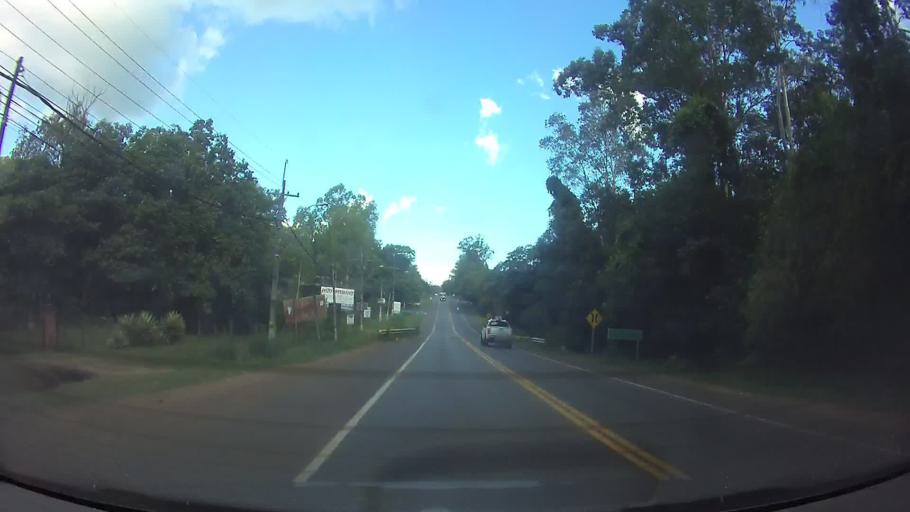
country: PY
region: Cordillera
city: Caacupe
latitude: -25.3854
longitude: -57.1227
